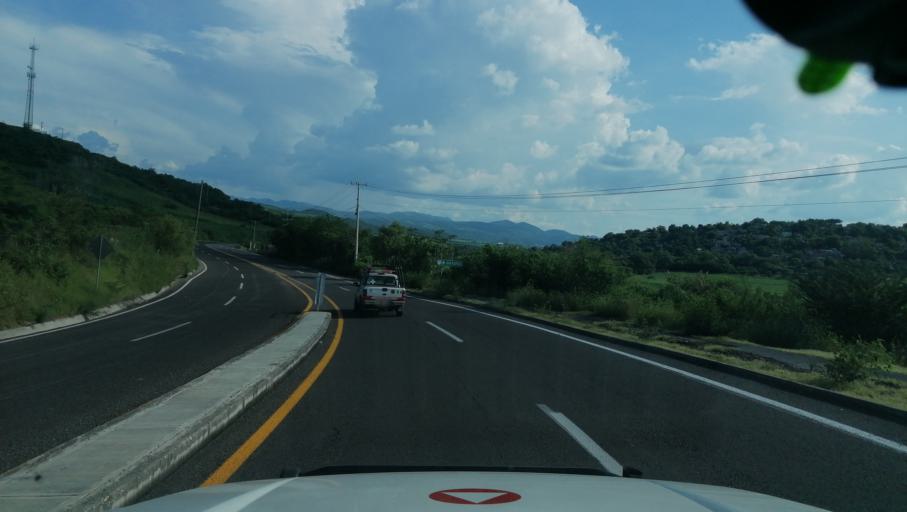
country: MX
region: Morelos
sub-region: Ayala
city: Abelardo L. Rodriguez
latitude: 18.6989
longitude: -98.9941
